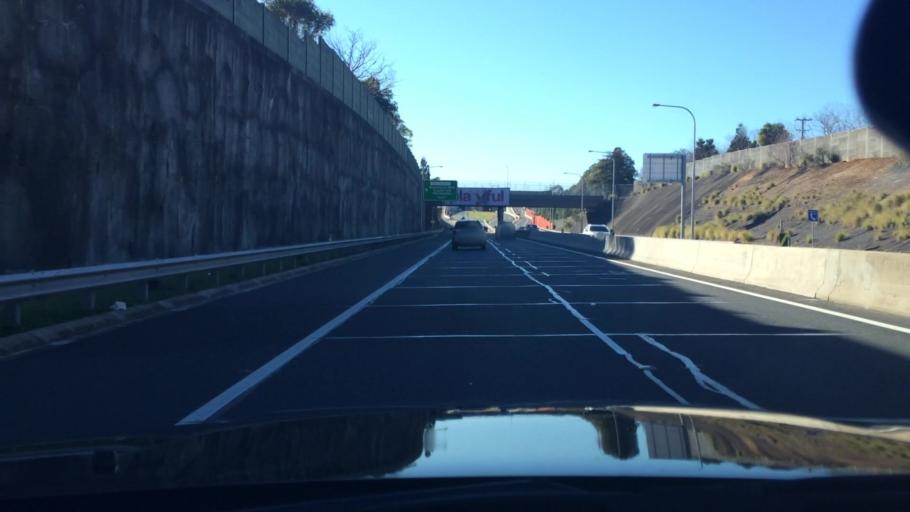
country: AU
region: New South Wales
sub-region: The Hills Shire
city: Baulkham Hills
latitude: -33.7698
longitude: 150.9902
